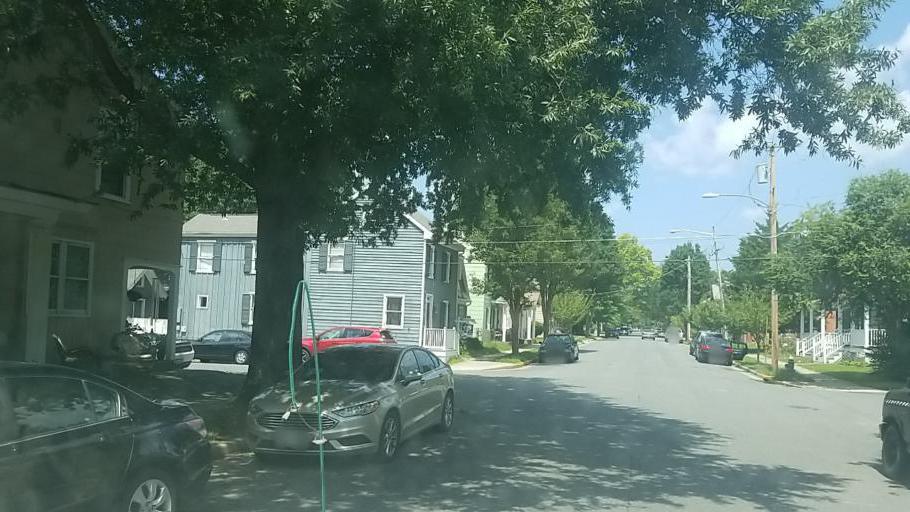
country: US
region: Maryland
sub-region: Talbot County
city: Easton
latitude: 38.7712
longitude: -76.0728
